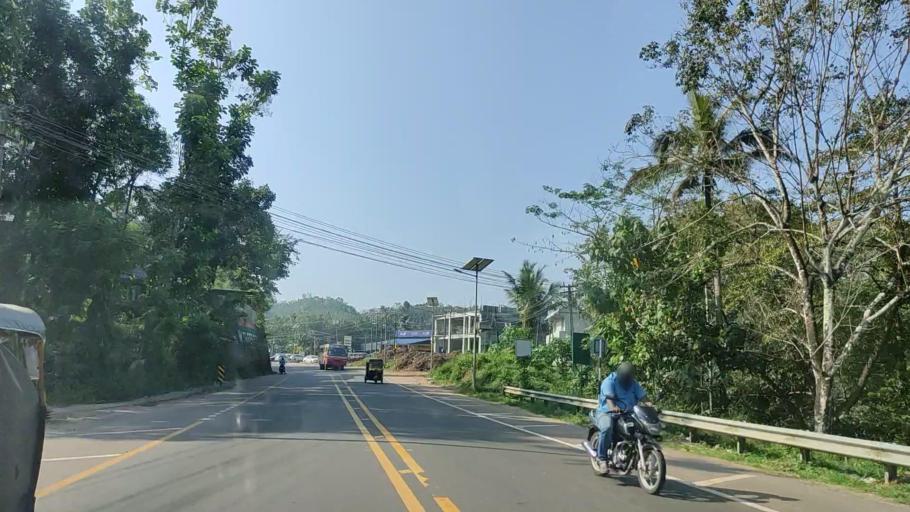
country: IN
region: Kerala
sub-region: Kollam
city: Punalur
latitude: 8.8795
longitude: 76.8670
